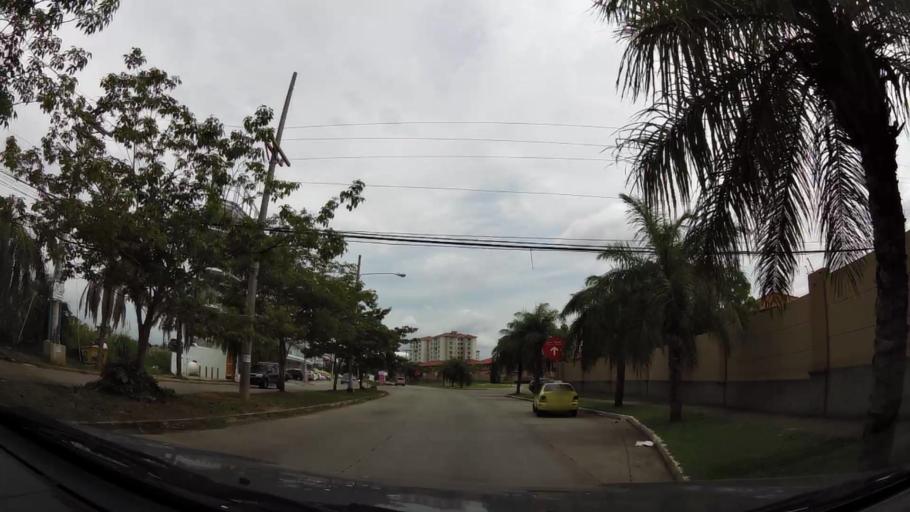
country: PA
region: Panama
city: San Miguelito
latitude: 9.0416
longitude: -79.4201
